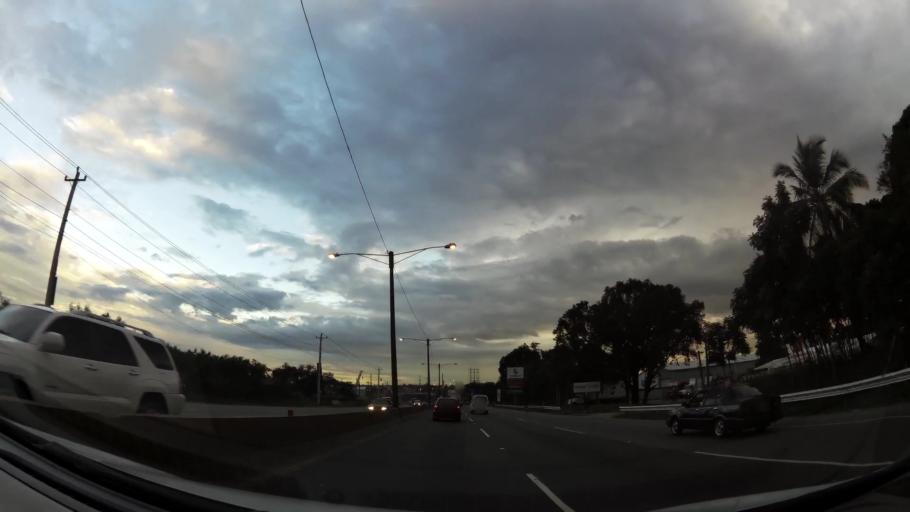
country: DO
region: Santo Domingo
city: Santo Domingo Oeste
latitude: 18.5427
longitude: -70.0355
